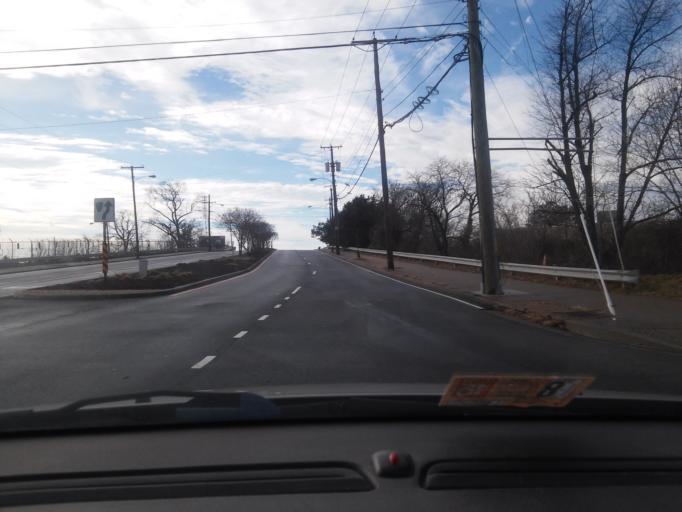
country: US
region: Virginia
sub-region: City of Richmond
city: Richmond
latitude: 37.5710
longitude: -77.4657
